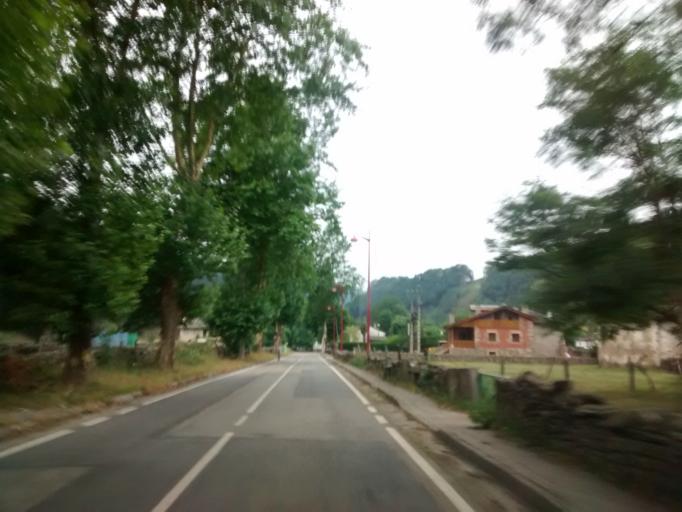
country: ES
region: Cantabria
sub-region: Provincia de Cantabria
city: Vega de Pas
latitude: 43.1577
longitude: -3.7993
